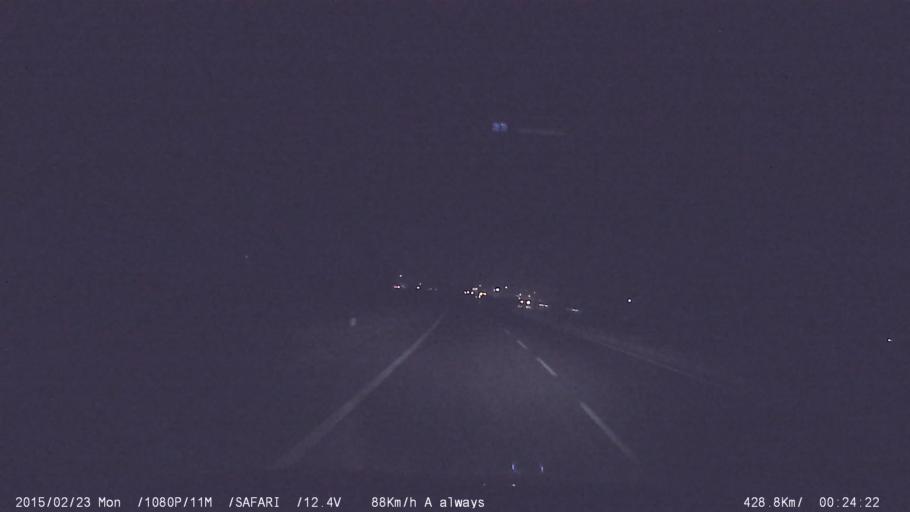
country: IN
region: Tamil Nadu
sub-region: Dharmapuri
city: Mallapuram
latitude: 11.9348
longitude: 78.0626
